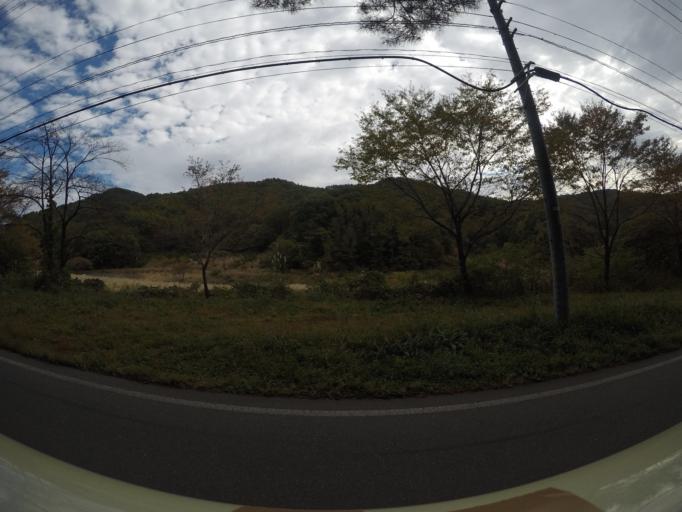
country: JP
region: Nagano
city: Chino
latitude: 35.9519
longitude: 138.1078
